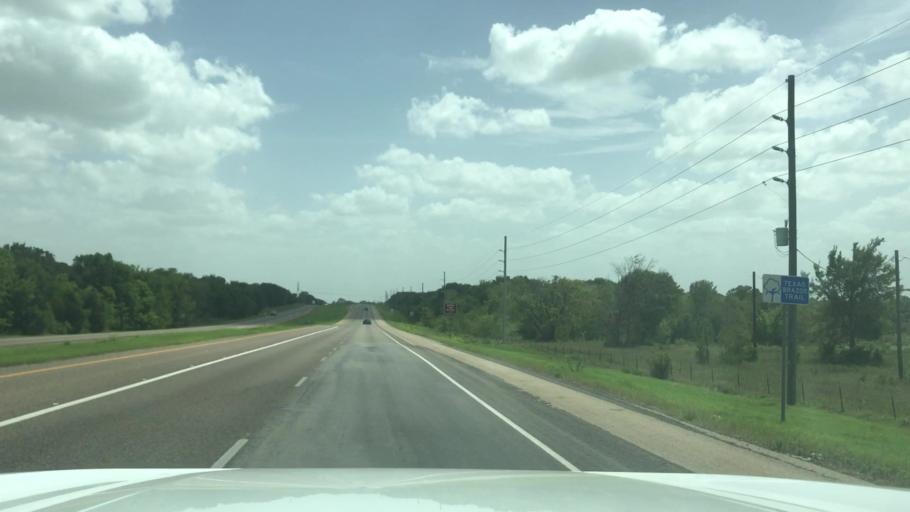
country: US
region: Texas
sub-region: Robertson County
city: Calvert
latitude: 31.1106
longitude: -96.7132
